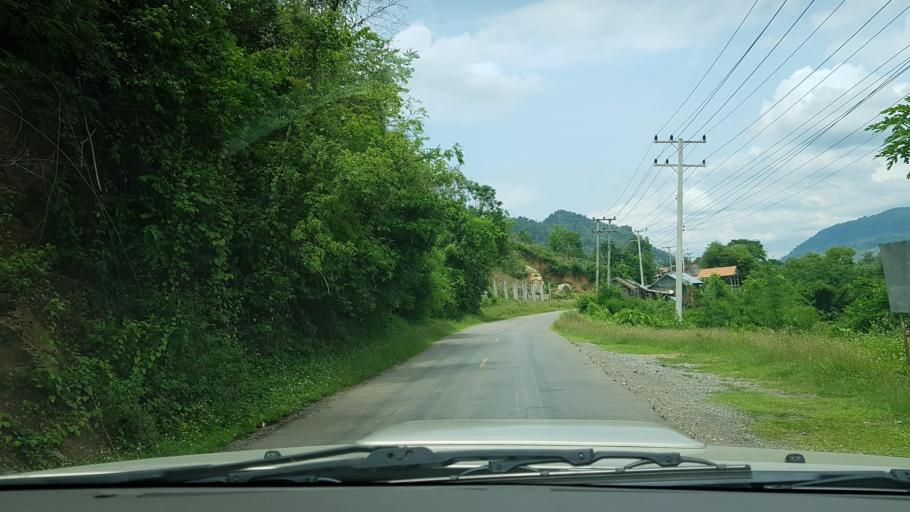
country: TH
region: Nan
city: Chaloem Phra Kiat
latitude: 19.9612
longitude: 101.2602
